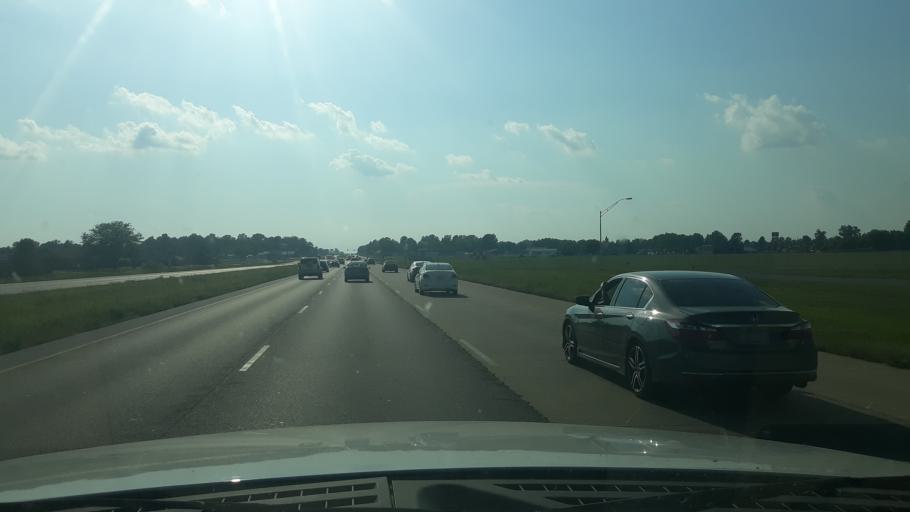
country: US
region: Illinois
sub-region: Williamson County
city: Energy
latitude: 37.7451
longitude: -89.0152
